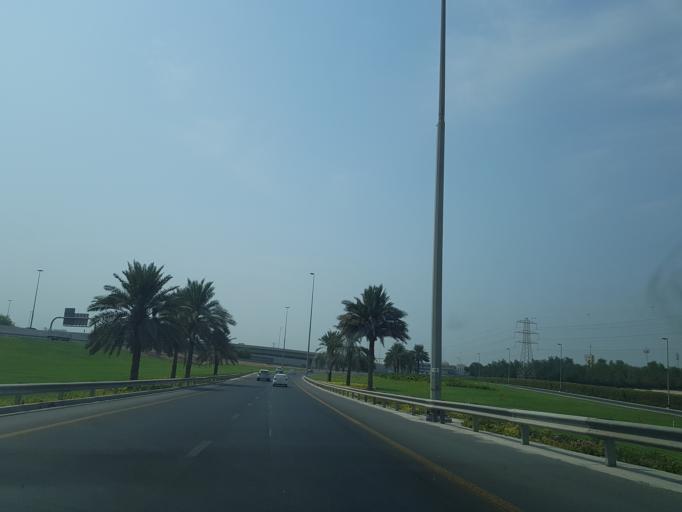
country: AE
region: Ash Shariqah
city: Sharjah
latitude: 25.2173
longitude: 55.3781
